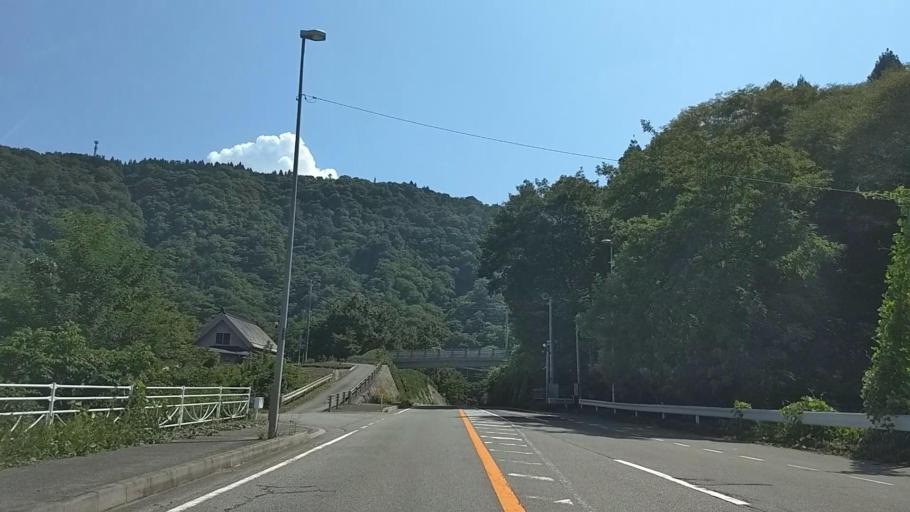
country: JP
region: Yamanashi
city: Ryuo
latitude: 35.5115
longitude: 138.4572
